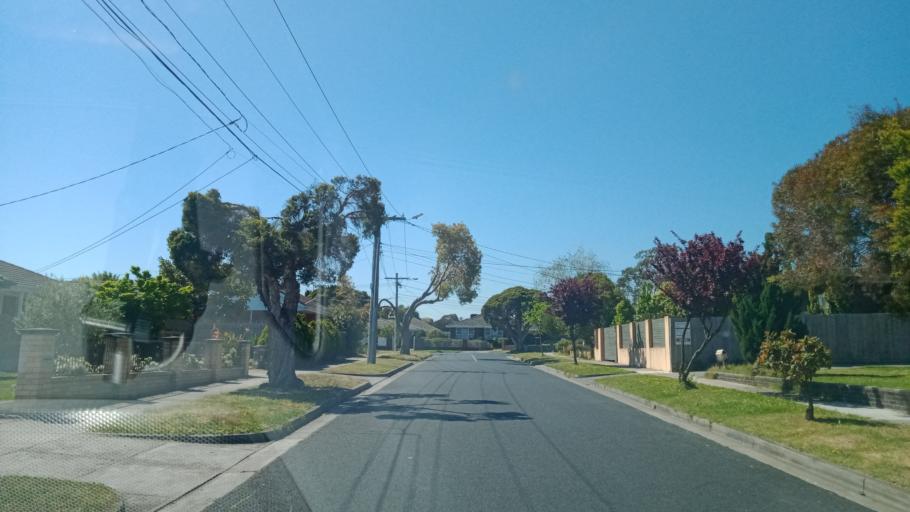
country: AU
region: Victoria
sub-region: Monash
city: Oakleigh South
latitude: -37.9307
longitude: 145.0841
